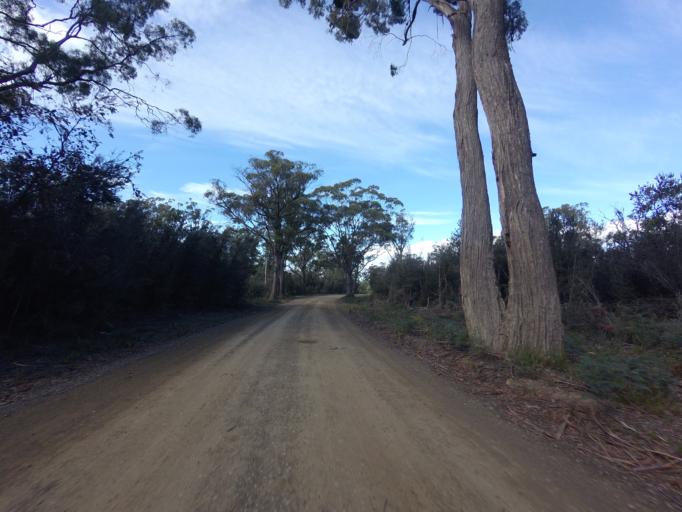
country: AU
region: Tasmania
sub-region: Clarence
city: Sandford
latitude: -42.9866
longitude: 147.7133
